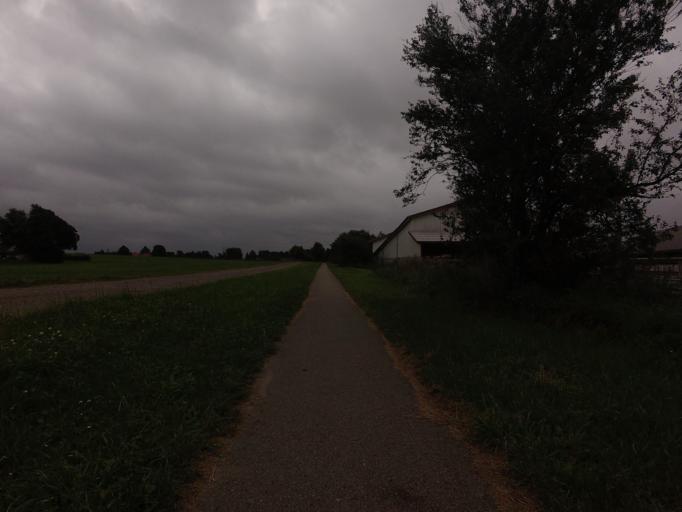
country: DK
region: Central Jutland
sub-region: Horsens Kommune
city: Braedstrup
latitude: 55.9848
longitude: 9.5935
